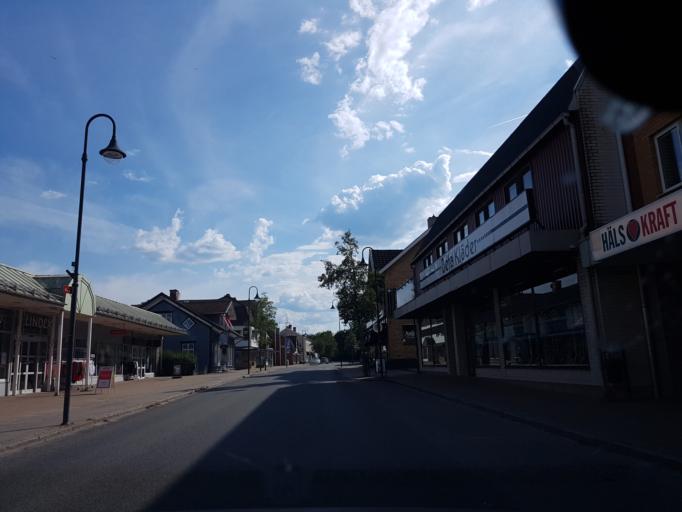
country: SE
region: Joenkoeping
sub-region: Gislaveds Kommun
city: Gislaved
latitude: 57.3022
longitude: 13.5376
